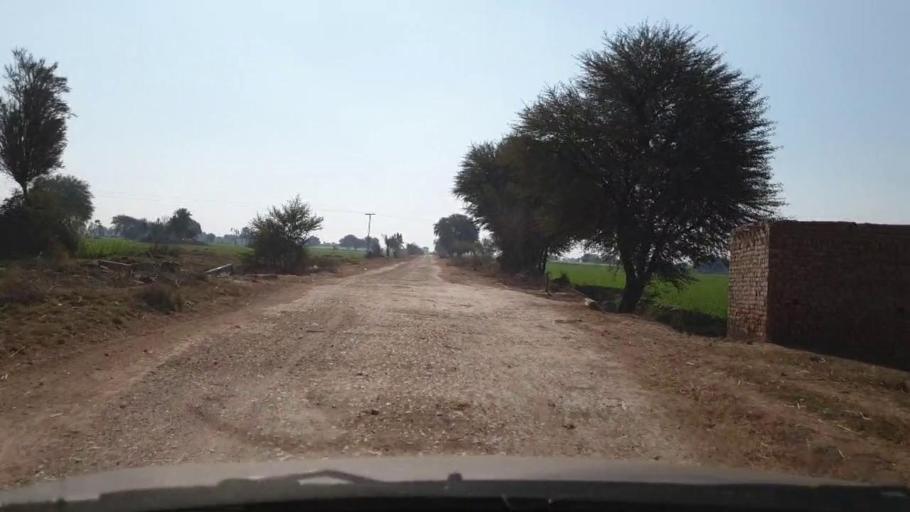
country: PK
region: Sindh
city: Jhol
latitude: 25.9365
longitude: 68.8004
